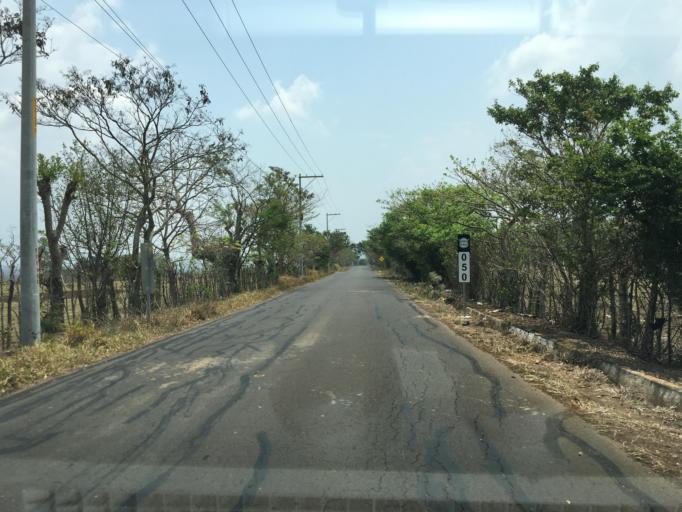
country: GT
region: Santa Rosa
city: Pueblo Nuevo Vinas
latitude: 14.3151
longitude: -90.5502
